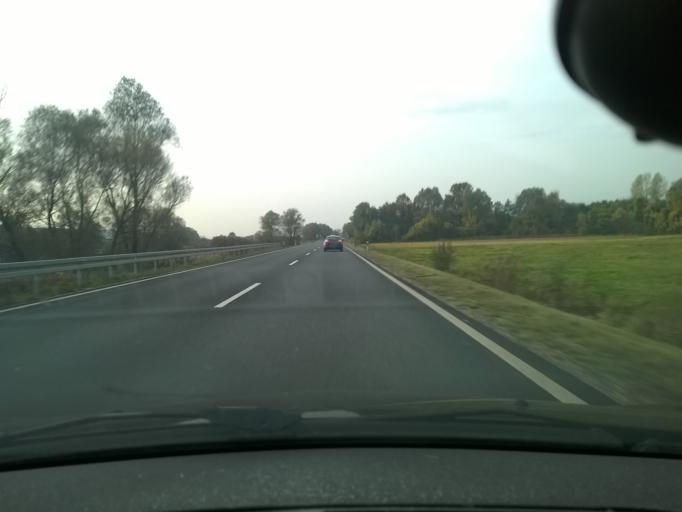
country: HR
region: Zagrebacka
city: Pojatno
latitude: 45.9171
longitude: 15.8194
